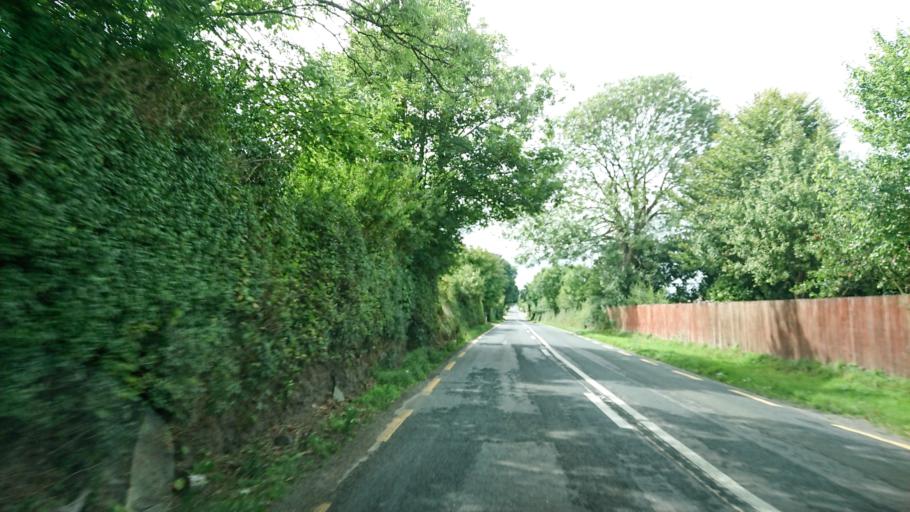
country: IE
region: Munster
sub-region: Waterford
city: Dungarvan
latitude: 52.1220
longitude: -7.7508
